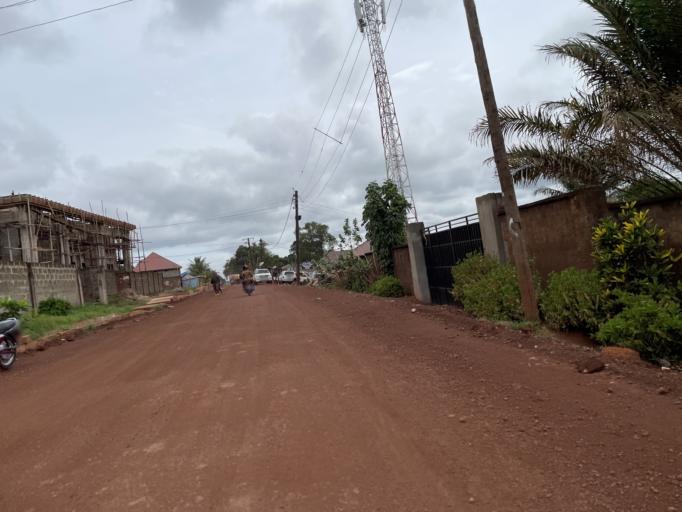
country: SL
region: Western Area
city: Hastings
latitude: 8.4018
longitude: -13.1443
